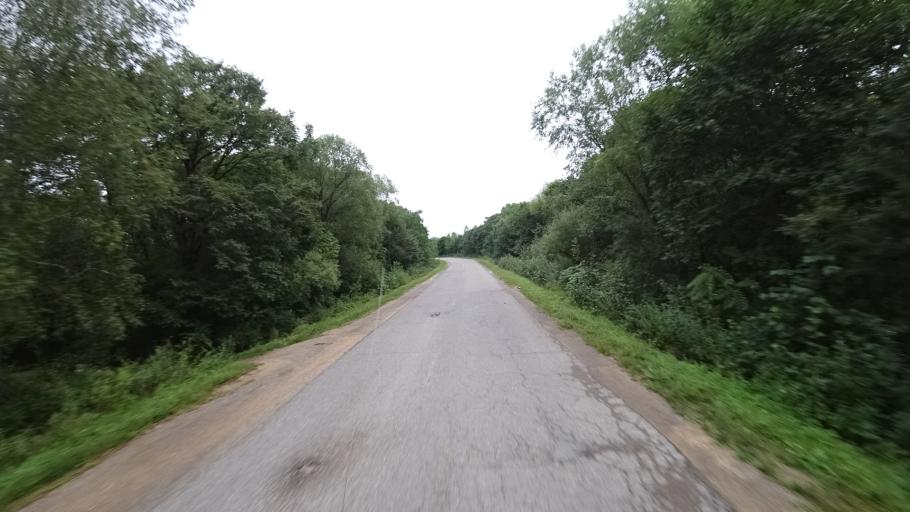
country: RU
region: Primorskiy
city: Rettikhovka
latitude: 44.1669
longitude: 132.7841
